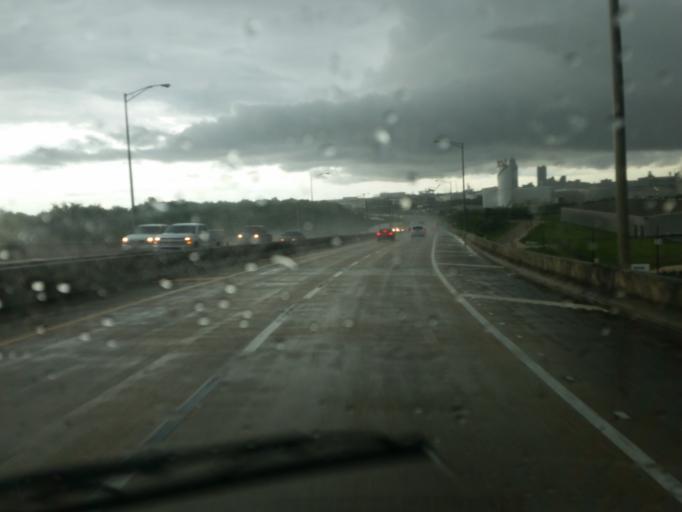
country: US
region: Alabama
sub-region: Mobile County
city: Mobile
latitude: 30.7297
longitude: -88.0373
